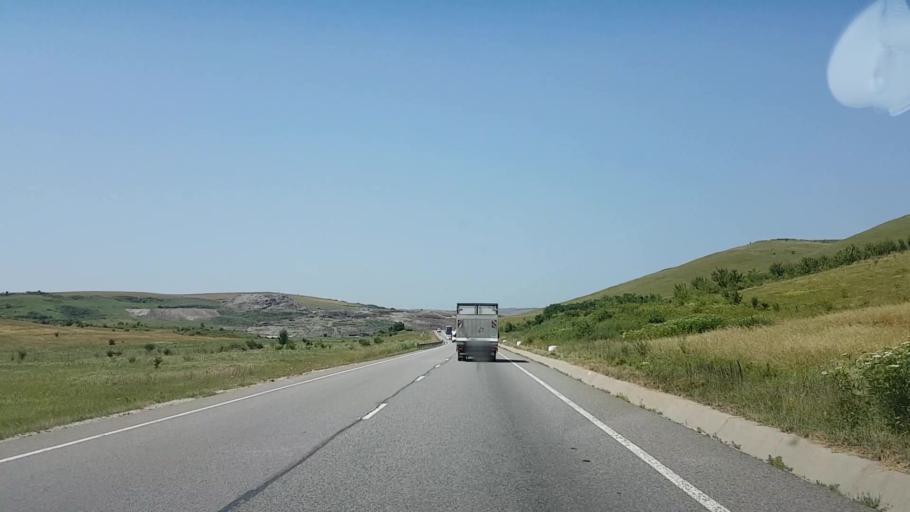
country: RO
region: Cluj
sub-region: Comuna Apahida
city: Dezmir
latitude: 46.7559
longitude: 23.6999
